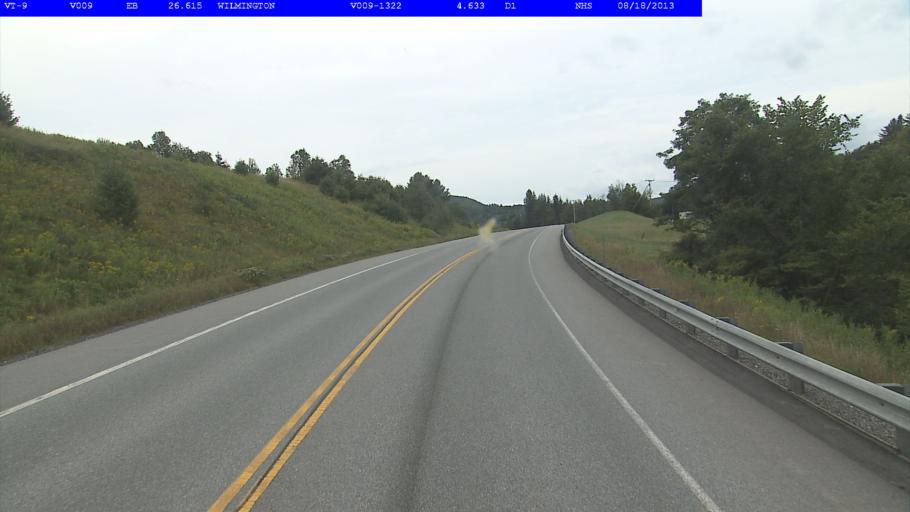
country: US
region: Vermont
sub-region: Windham County
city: Dover
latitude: 42.8601
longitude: -72.8432
